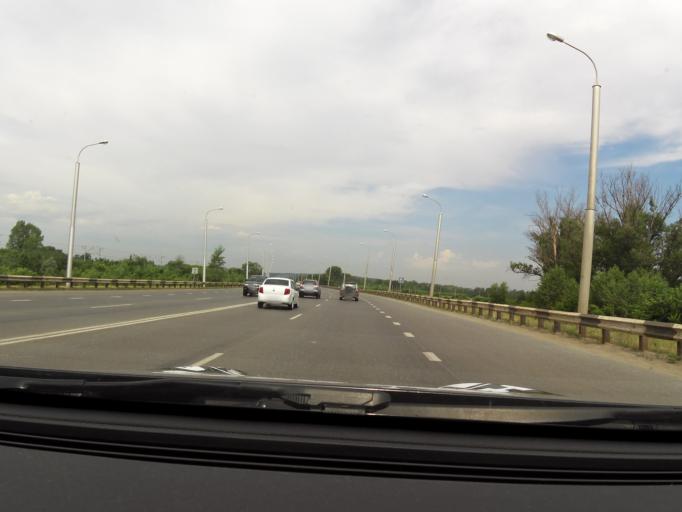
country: RU
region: Bashkortostan
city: Iglino
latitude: 54.7989
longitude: 56.2029
